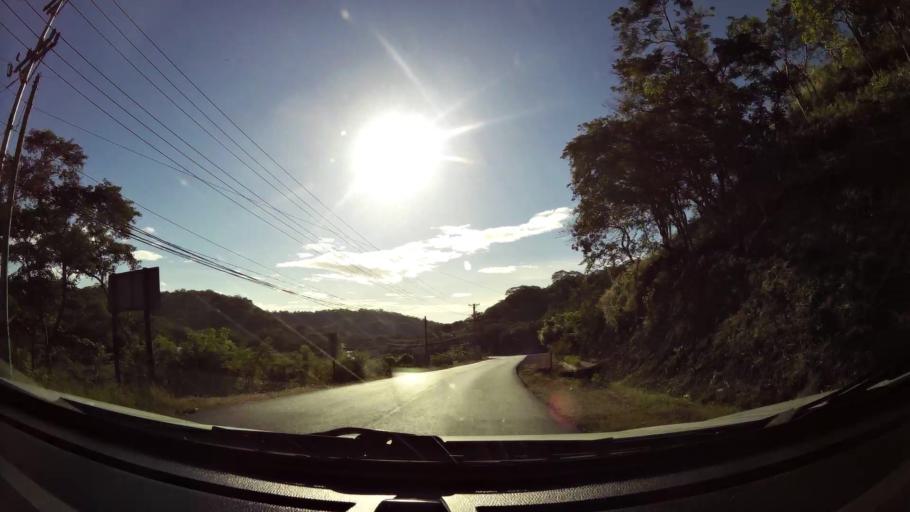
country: CR
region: Guanacaste
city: Sardinal
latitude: 10.5383
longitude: -85.6688
